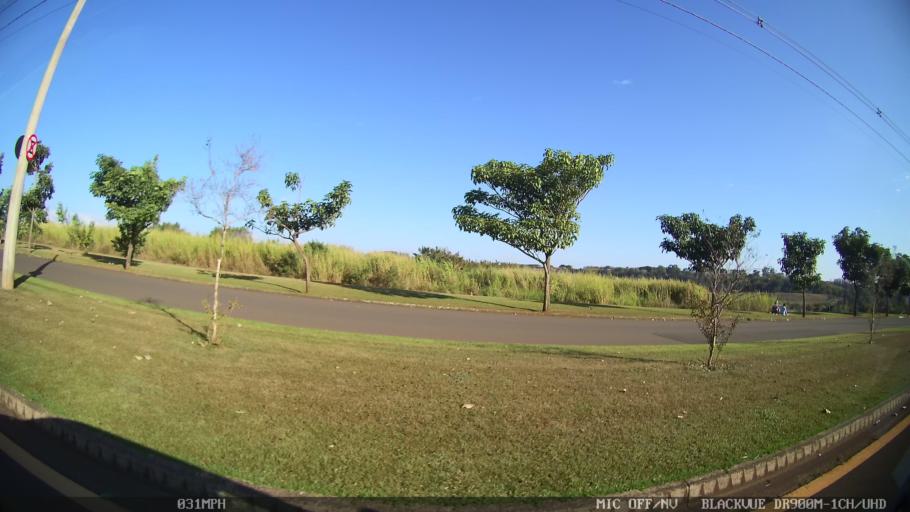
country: BR
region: Sao Paulo
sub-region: Piracicaba
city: Piracicaba
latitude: -22.6953
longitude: -47.6171
